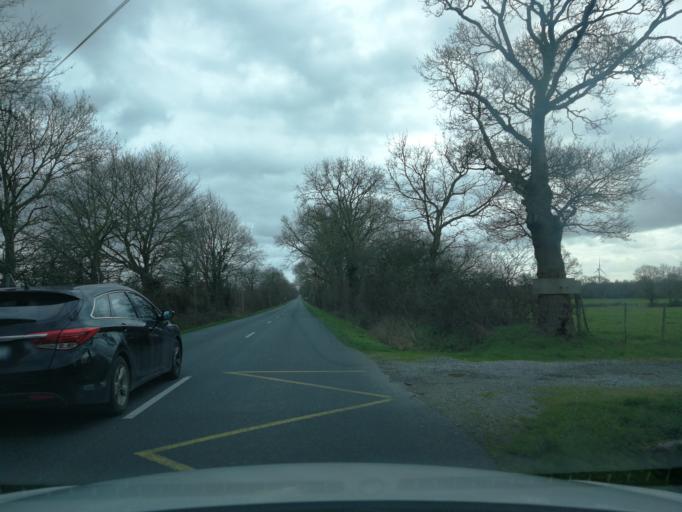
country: FR
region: Pays de la Loire
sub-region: Departement de la Loire-Atlantique
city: Montbert
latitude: 47.0218
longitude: -1.4903
